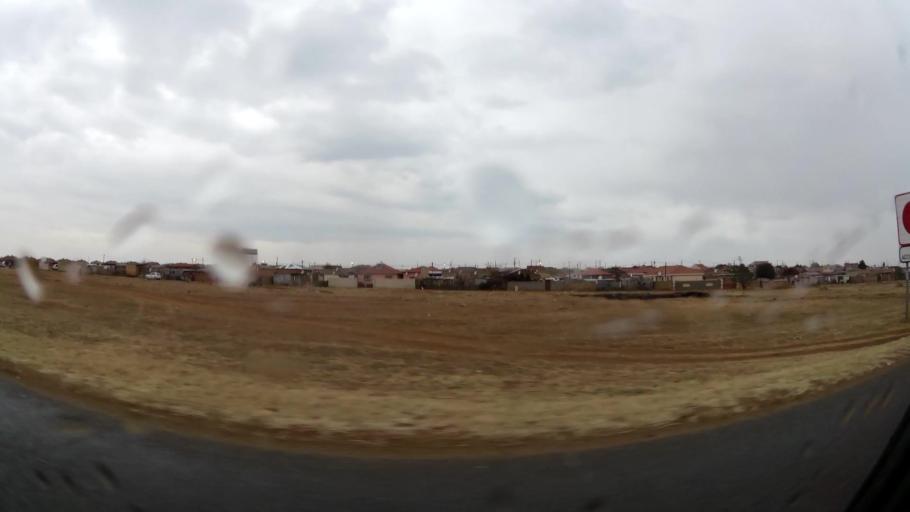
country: ZA
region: Gauteng
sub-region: City of Johannesburg Metropolitan Municipality
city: Roodepoort
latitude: -26.1719
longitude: 27.7959
